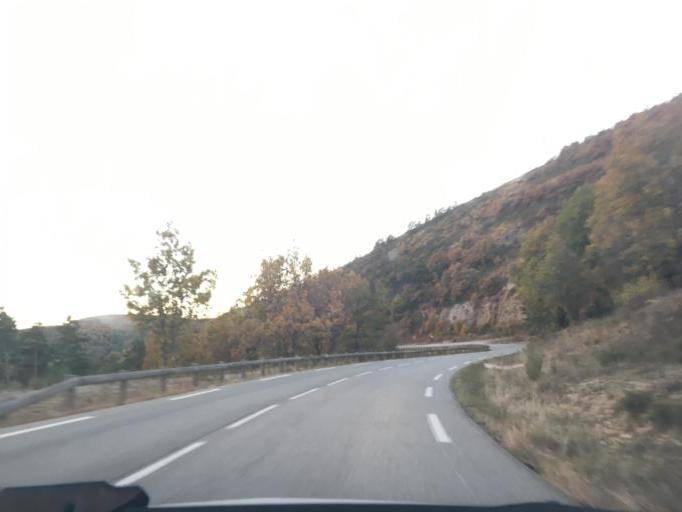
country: FR
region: Provence-Alpes-Cote d'Azur
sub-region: Departement du Var
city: Bargemon
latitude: 43.6900
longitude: 6.5077
